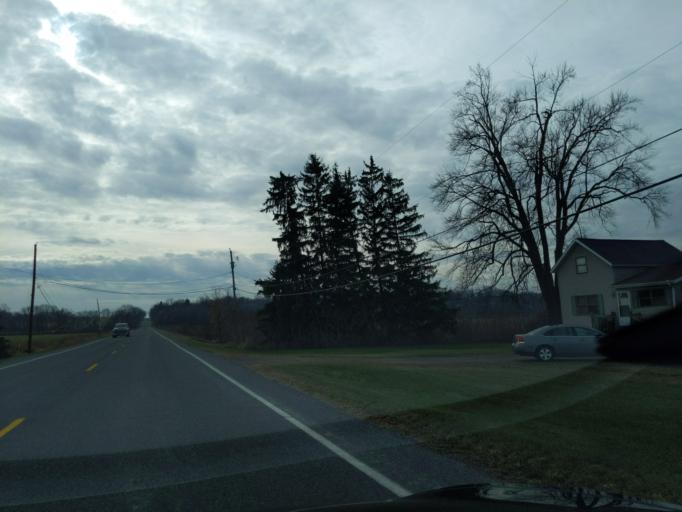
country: US
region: Michigan
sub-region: Ingham County
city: Holt
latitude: 42.5674
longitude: -84.5228
